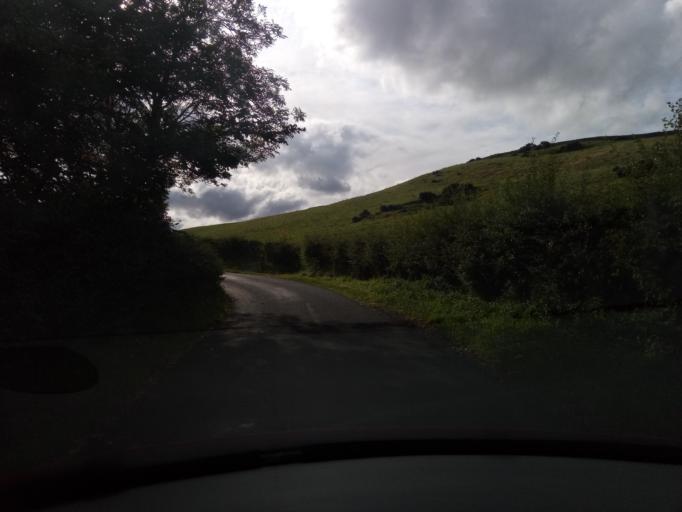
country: GB
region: Scotland
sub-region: The Scottish Borders
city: Kelso
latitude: 55.4853
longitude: -2.3488
